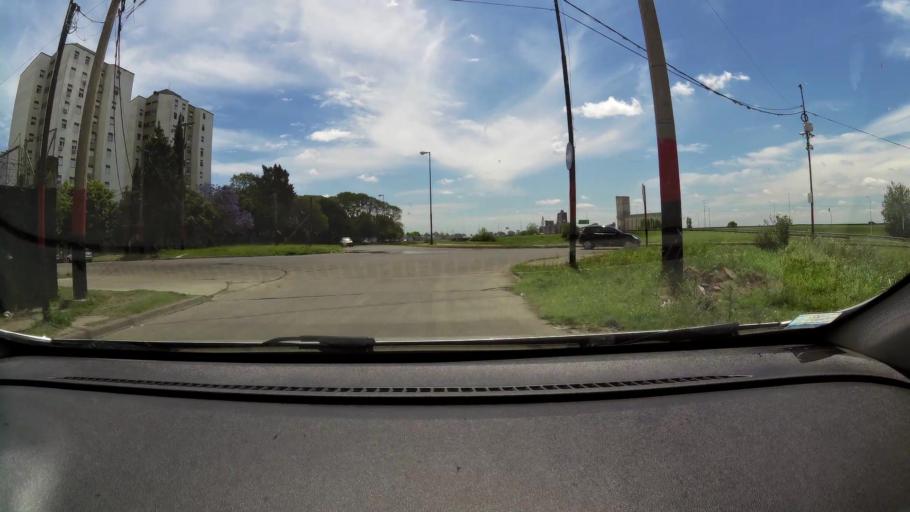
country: AR
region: Santa Fe
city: Gobernador Galvez
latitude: -32.9934
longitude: -60.6214
